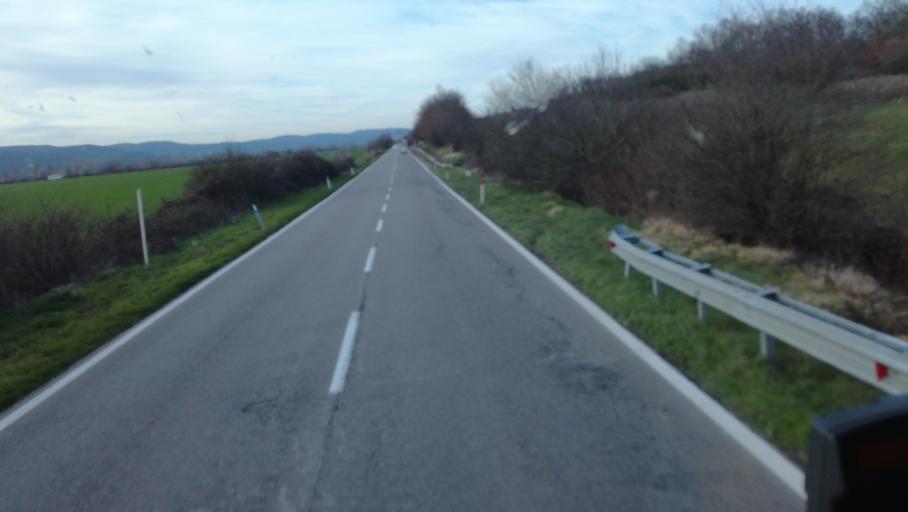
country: IT
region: Tuscany
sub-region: Provincia di Siena
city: Rosia
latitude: 43.2134
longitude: 11.2775
